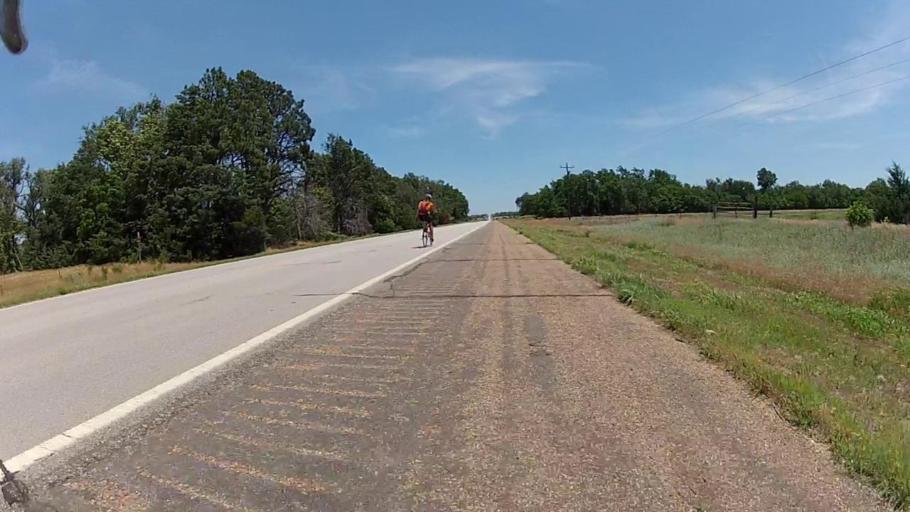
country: US
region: Kansas
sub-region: Barber County
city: Medicine Lodge
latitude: 37.2533
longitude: -98.3263
